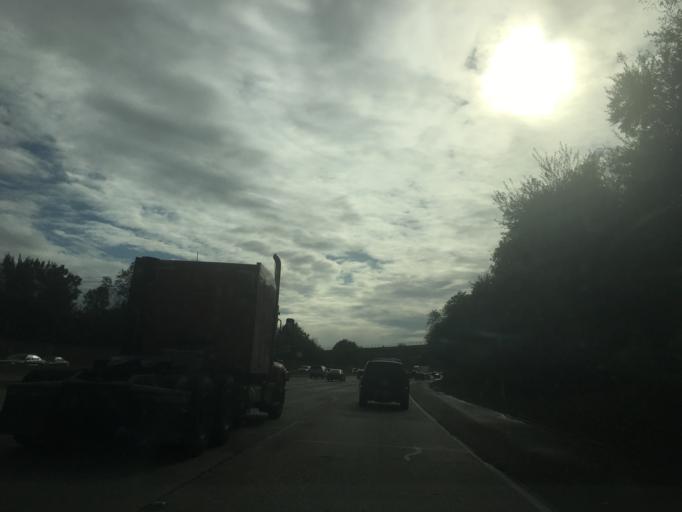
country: US
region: California
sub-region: Sacramento County
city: Sacramento
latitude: 38.5467
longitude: -121.5101
